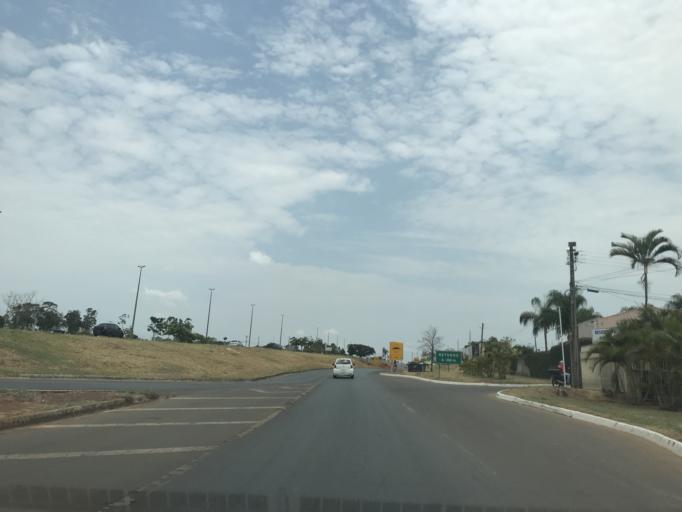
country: BR
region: Federal District
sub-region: Brasilia
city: Brasilia
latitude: -15.6806
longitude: -47.8353
